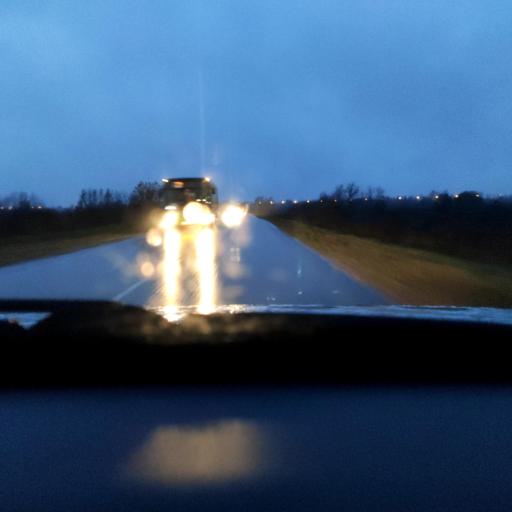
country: RU
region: Perm
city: Kondratovo
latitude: 57.9951
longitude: 56.0873
